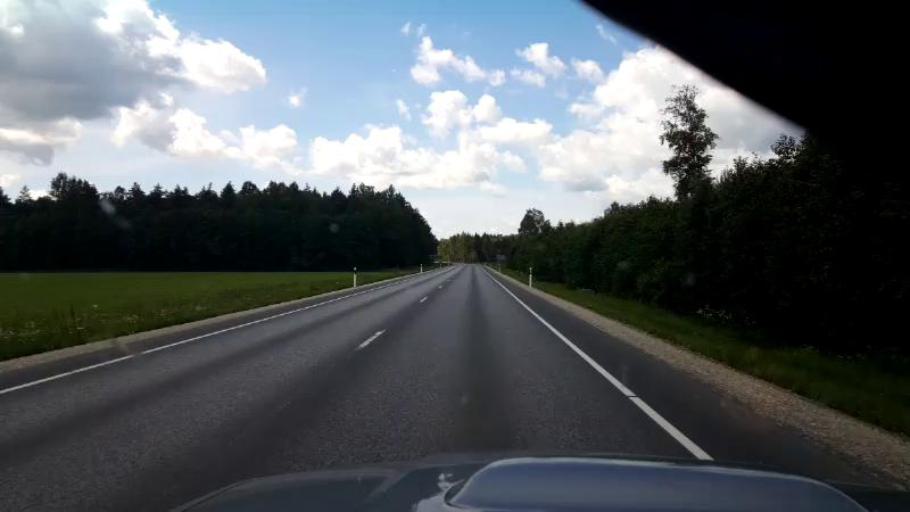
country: EE
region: Jaervamaa
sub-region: Paide linn
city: Paide
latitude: 59.0074
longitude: 25.6873
